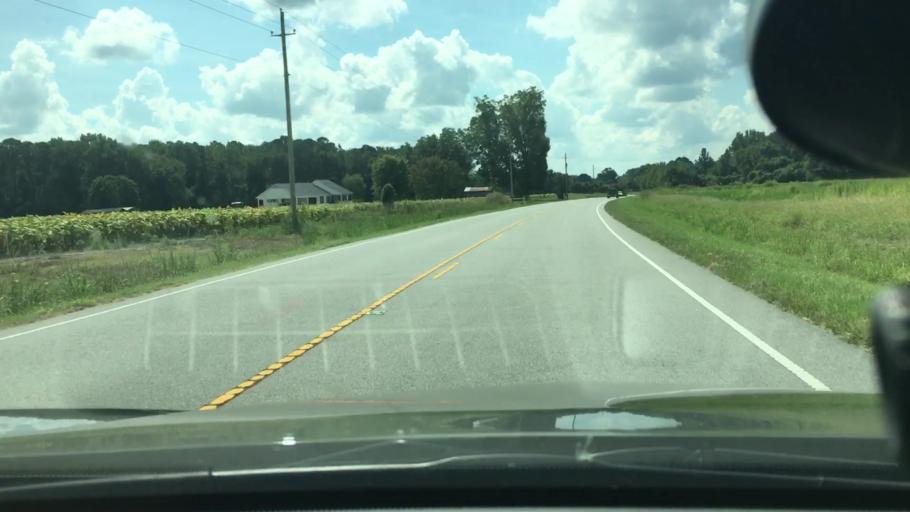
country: US
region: North Carolina
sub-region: Pitt County
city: Farmville
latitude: 35.7075
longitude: -77.5185
